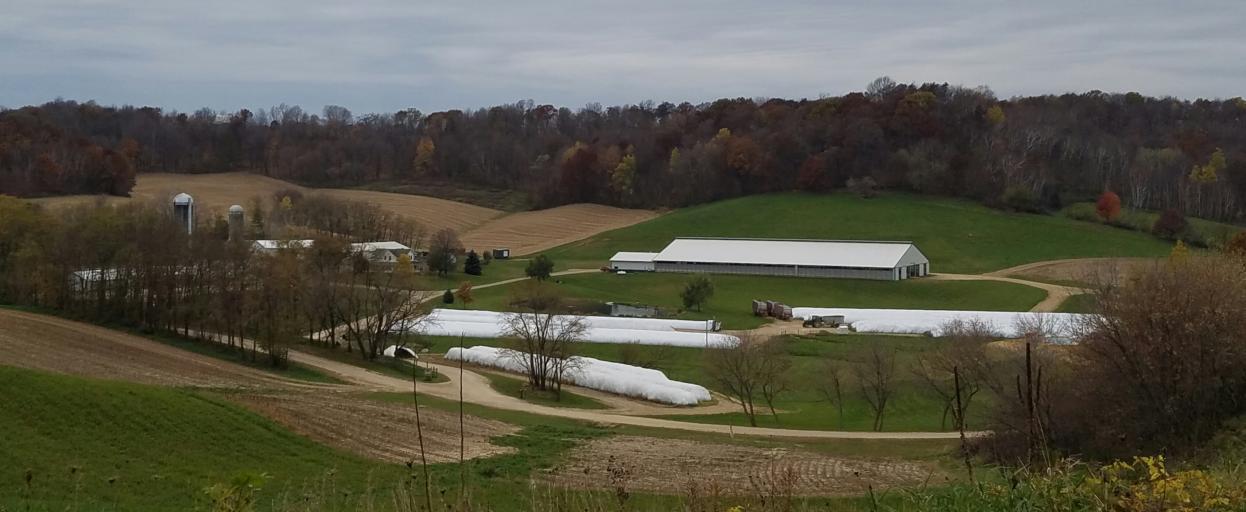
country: US
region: Wisconsin
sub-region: Vernon County
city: Hillsboro
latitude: 43.6317
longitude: -90.3134
